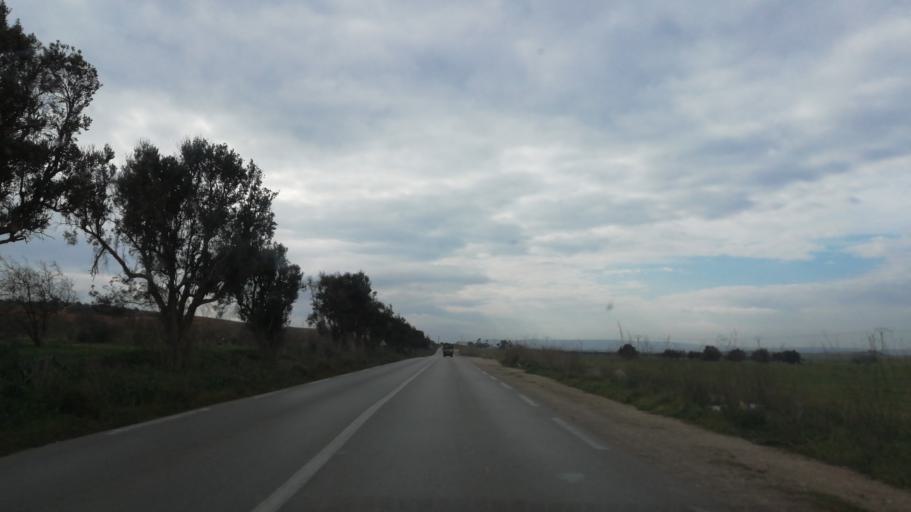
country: DZ
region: Oran
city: Ain el Bya
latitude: 35.7532
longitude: -0.3514
